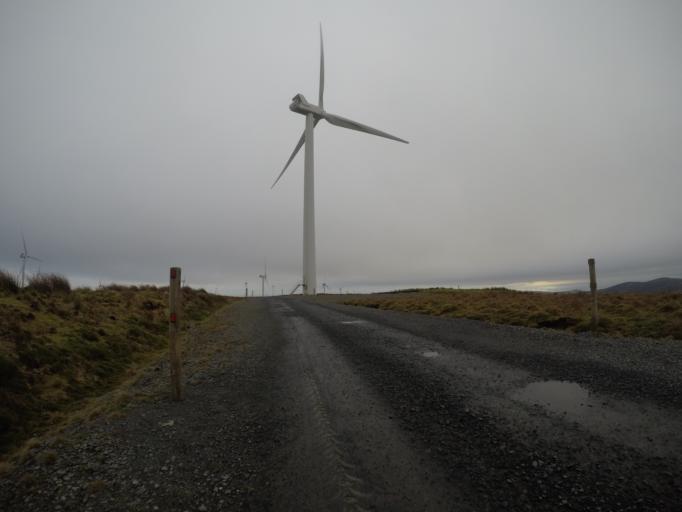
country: GB
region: Scotland
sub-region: North Ayrshire
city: Fairlie
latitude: 55.7442
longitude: -4.7969
